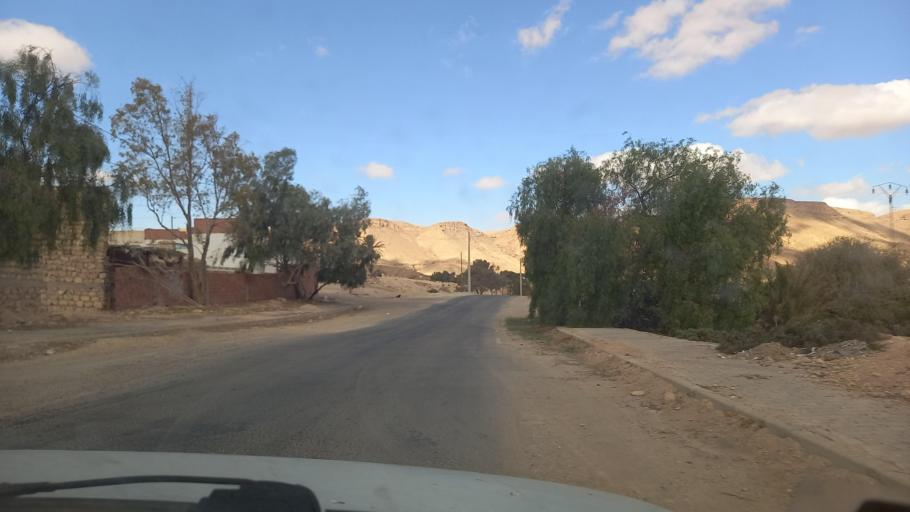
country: TN
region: Tataouine
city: Tataouine
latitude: 32.9150
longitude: 10.2778
